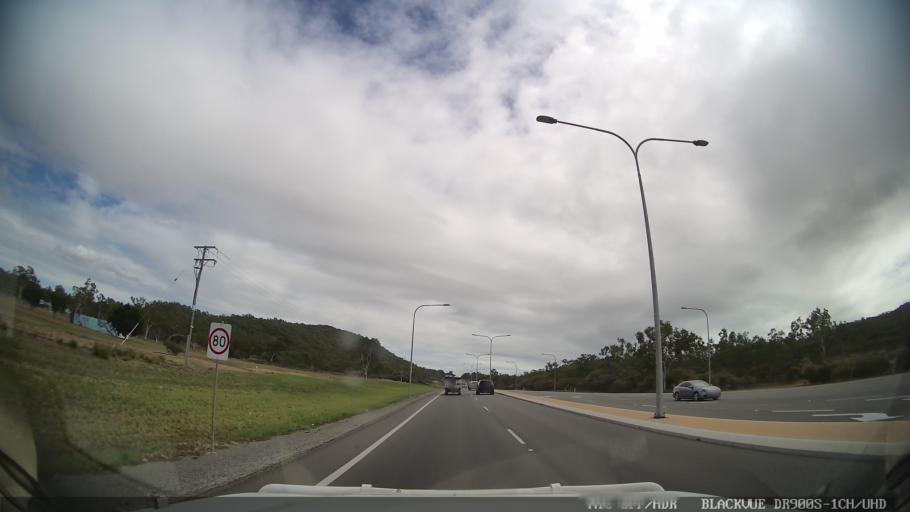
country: AU
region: Queensland
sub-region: Townsville
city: Townsville
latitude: -19.3713
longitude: 146.8979
